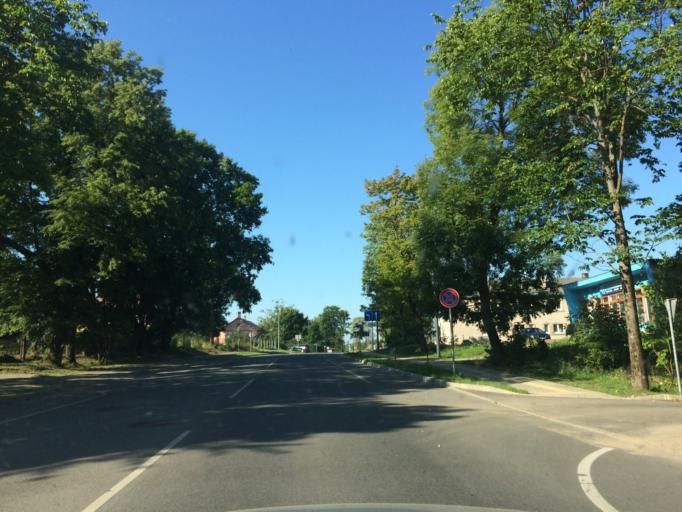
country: LV
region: Rezekne
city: Rezekne
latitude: 56.4968
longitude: 27.3238
